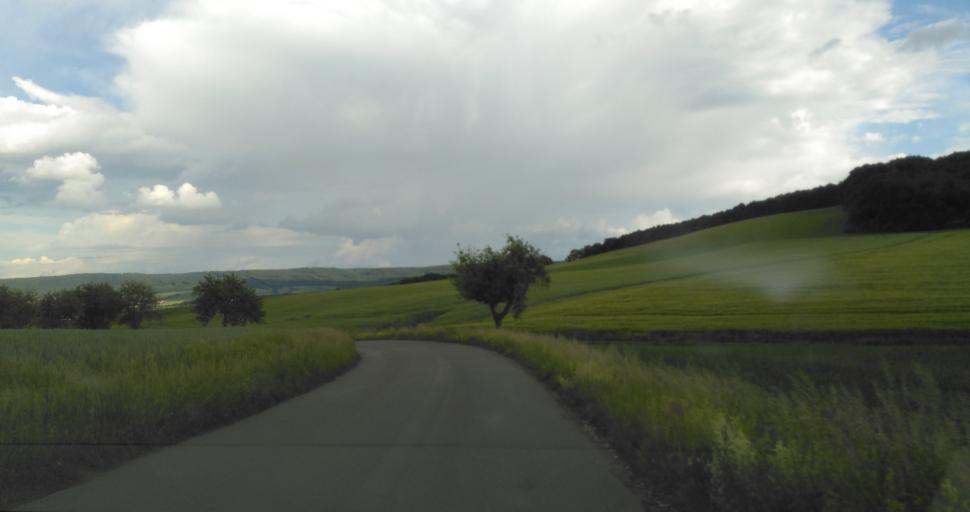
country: CZ
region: Central Bohemia
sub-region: Okres Beroun
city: Beroun
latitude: 49.9224
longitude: 14.1282
